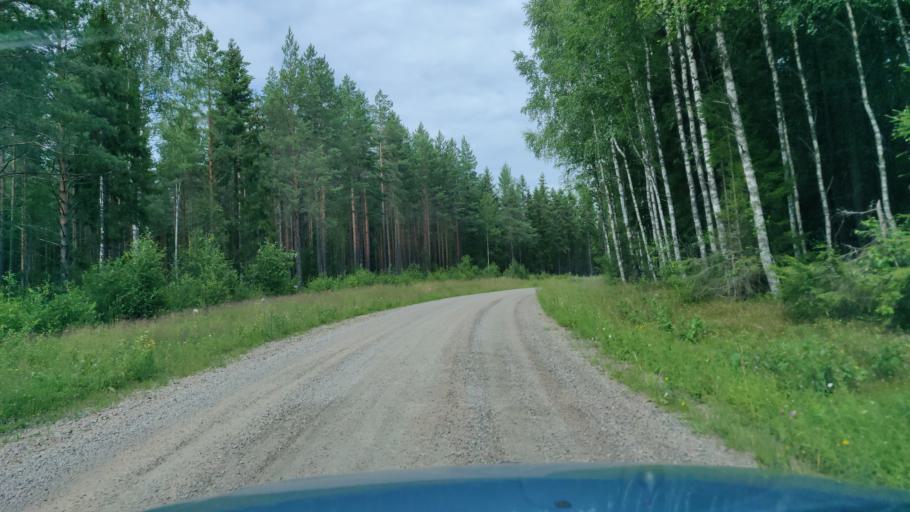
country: SE
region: Vaermland
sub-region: Munkfors Kommun
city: Munkfors
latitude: 59.9397
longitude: 13.5941
